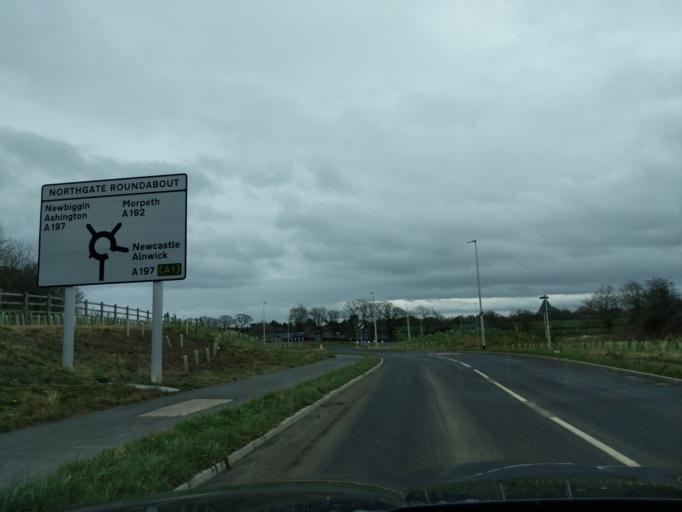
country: GB
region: England
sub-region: Northumberland
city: Morpeth
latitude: 55.1798
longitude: -1.7125
